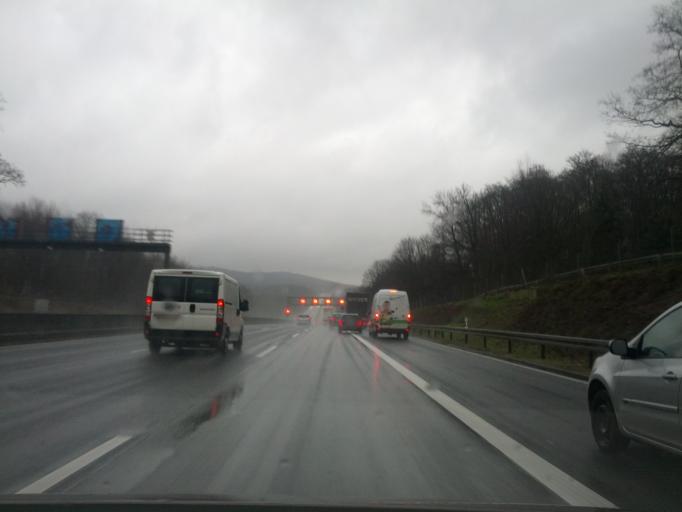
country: DE
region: Hesse
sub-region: Regierungsbezirk Darmstadt
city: Rosbach vor der Hohe
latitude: 50.2791
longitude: 8.6678
